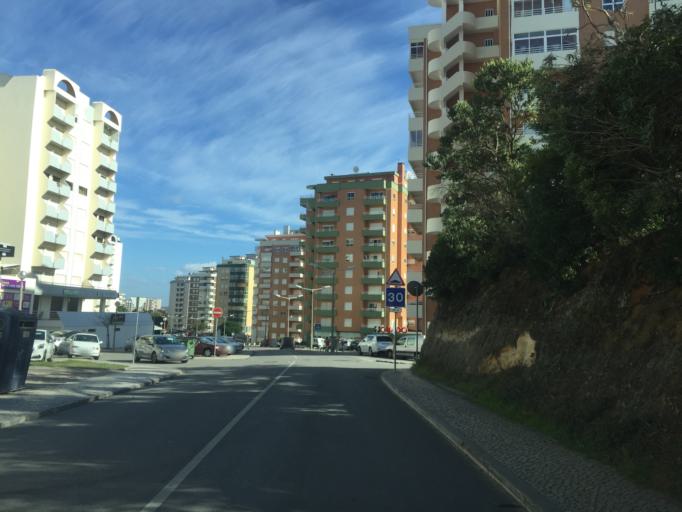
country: PT
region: Coimbra
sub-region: Figueira da Foz
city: Buarcos
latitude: 40.1634
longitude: -8.8658
